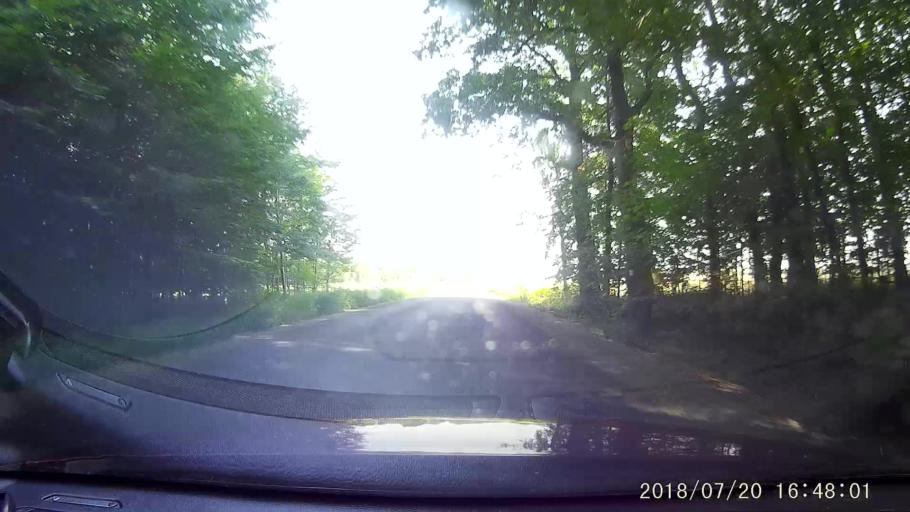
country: PL
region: Lower Silesian Voivodeship
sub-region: Powiat lubanski
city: Siekierczyn
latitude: 51.0589
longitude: 15.1853
